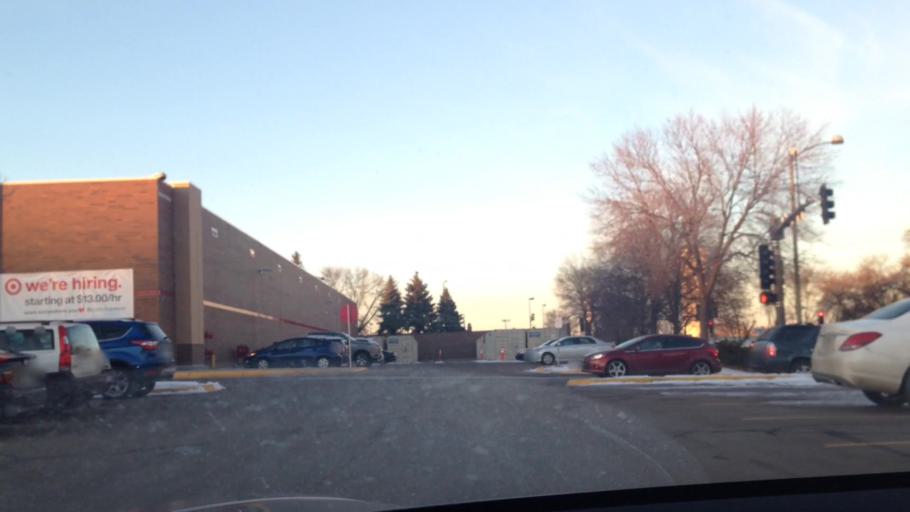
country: US
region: Minnesota
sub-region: Hennepin County
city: Saint Louis Park
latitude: 44.9366
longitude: -93.3459
